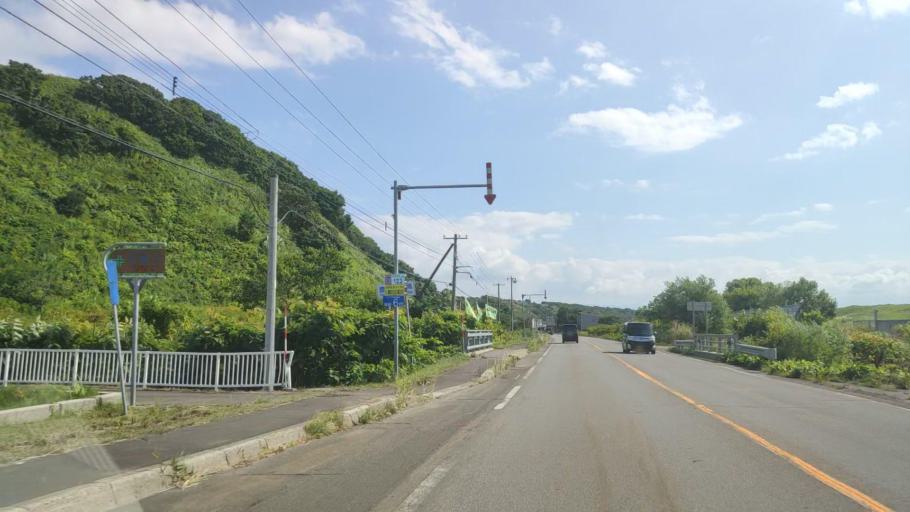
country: JP
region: Hokkaido
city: Rumoi
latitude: 43.9744
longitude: 141.6465
